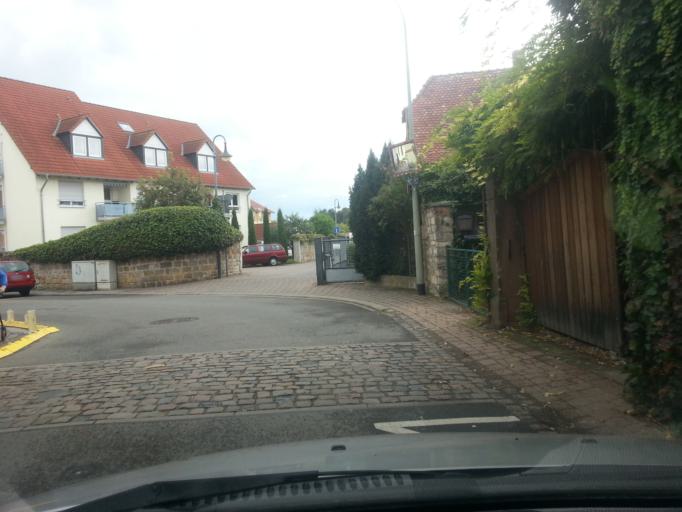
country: DE
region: Rheinland-Pfalz
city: Freinsheim
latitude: 49.5060
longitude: 8.2160
